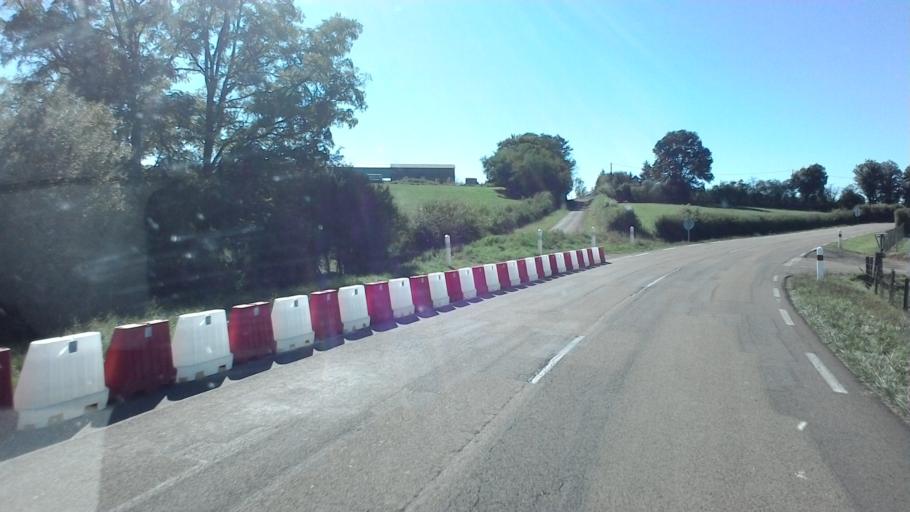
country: FR
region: Bourgogne
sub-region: Departement de la Cote-d'Or
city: Semur-en-Auxois
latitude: 47.4012
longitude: 4.3060
